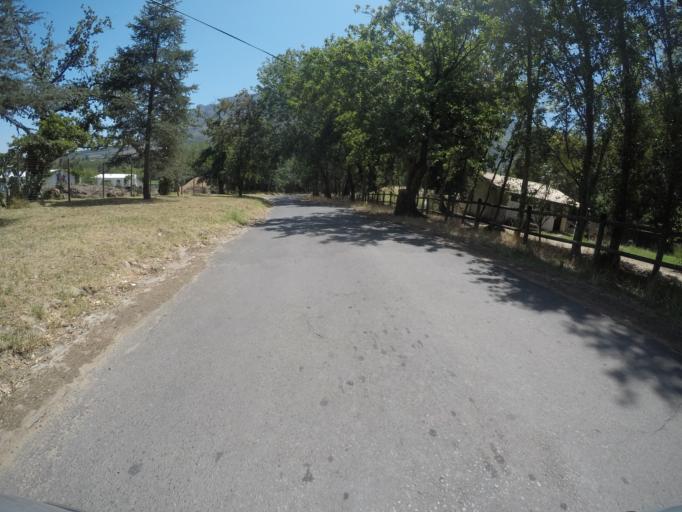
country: ZA
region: Western Cape
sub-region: Cape Winelands District Municipality
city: Stellenbosch
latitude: -33.9962
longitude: 18.8758
